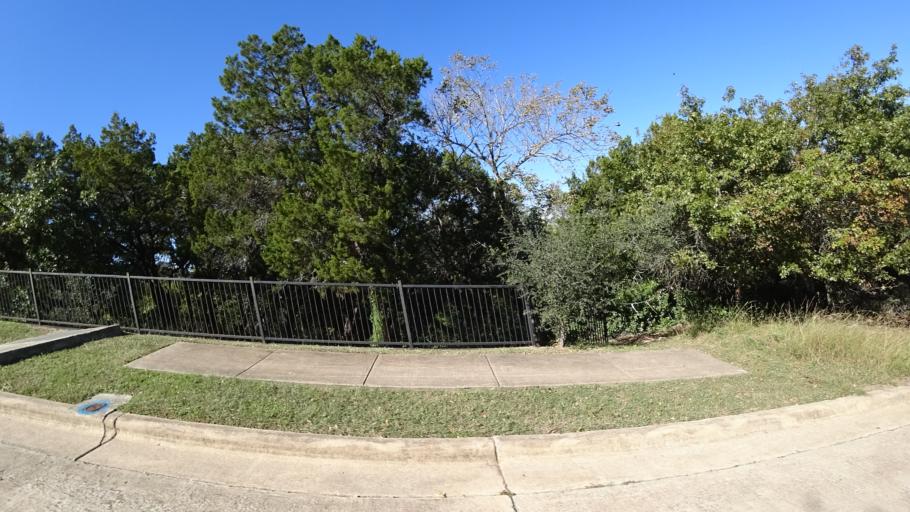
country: US
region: Texas
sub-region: Travis County
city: West Lake Hills
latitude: 30.3543
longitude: -97.7794
